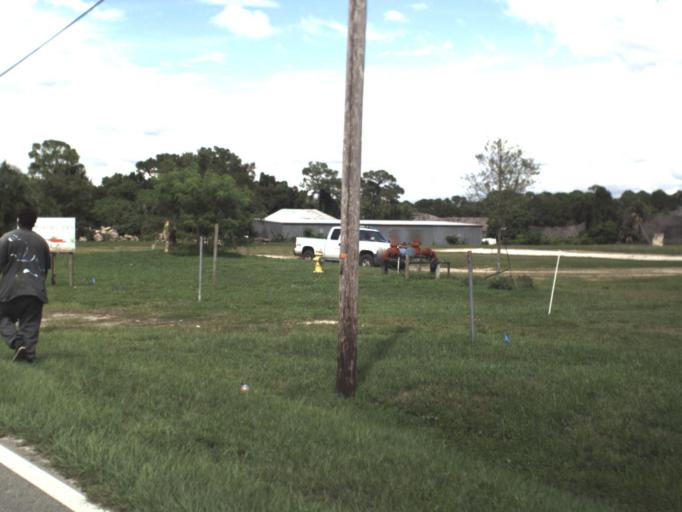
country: US
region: Florida
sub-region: Manatee County
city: Samoset
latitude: 27.4529
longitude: -82.5467
